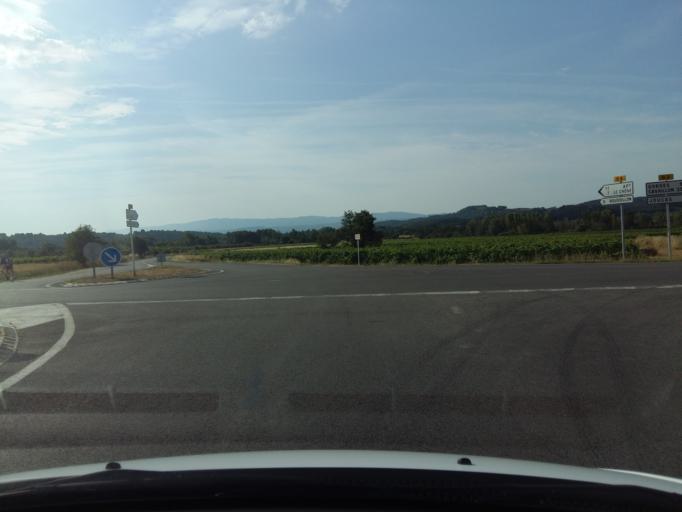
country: FR
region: Provence-Alpes-Cote d'Azur
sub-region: Departement du Vaucluse
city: Roussillon
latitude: 43.9274
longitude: 5.2950
